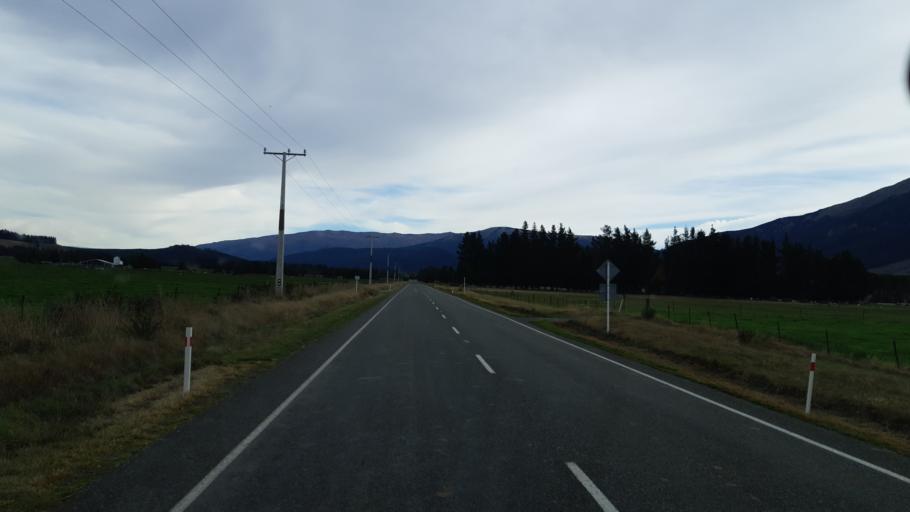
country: NZ
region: Tasman
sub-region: Tasman District
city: Brightwater
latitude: -41.6532
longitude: 173.2758
